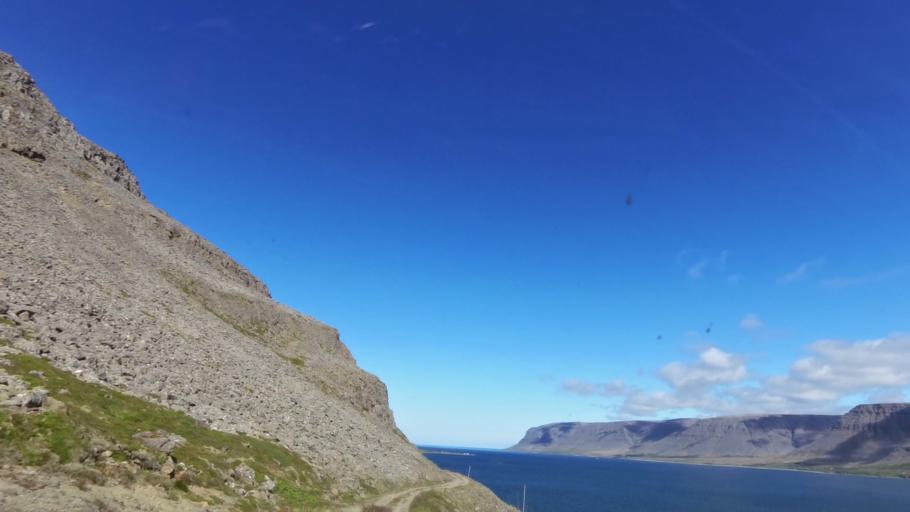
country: IS
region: West
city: Olafsvik
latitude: 65.6229
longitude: -23.8841
